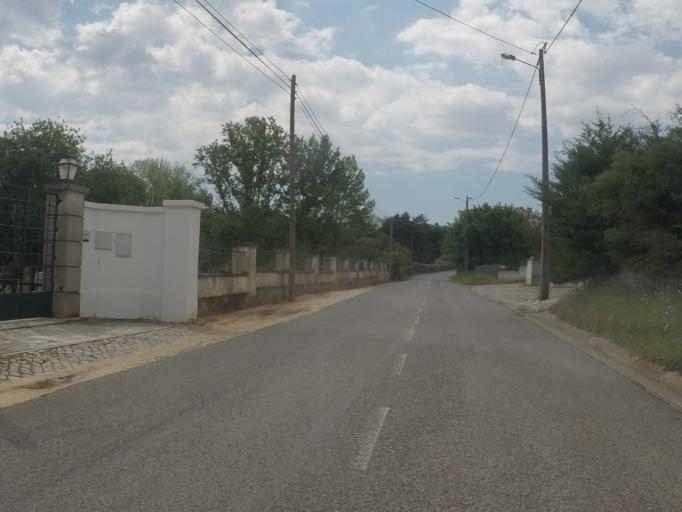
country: PT
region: Setubal
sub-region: Palmela
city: Quinta do Anjo
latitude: 38.4991
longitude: -8.9926
